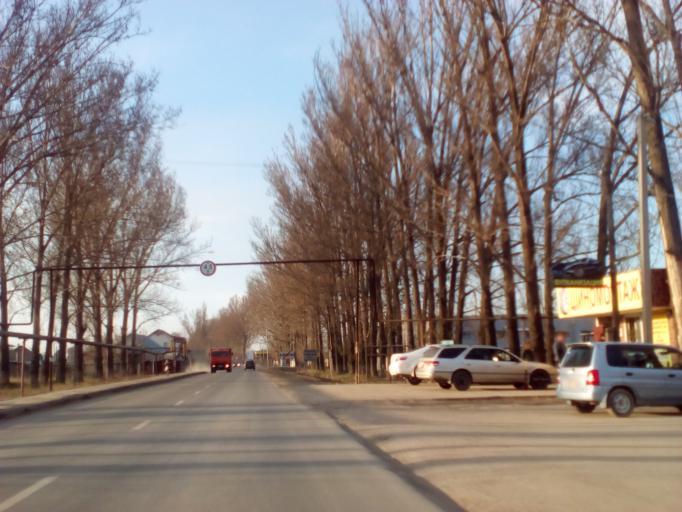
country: KZ
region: Almaty Oblysy
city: Burunday
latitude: 43.2504
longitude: 76.7841
